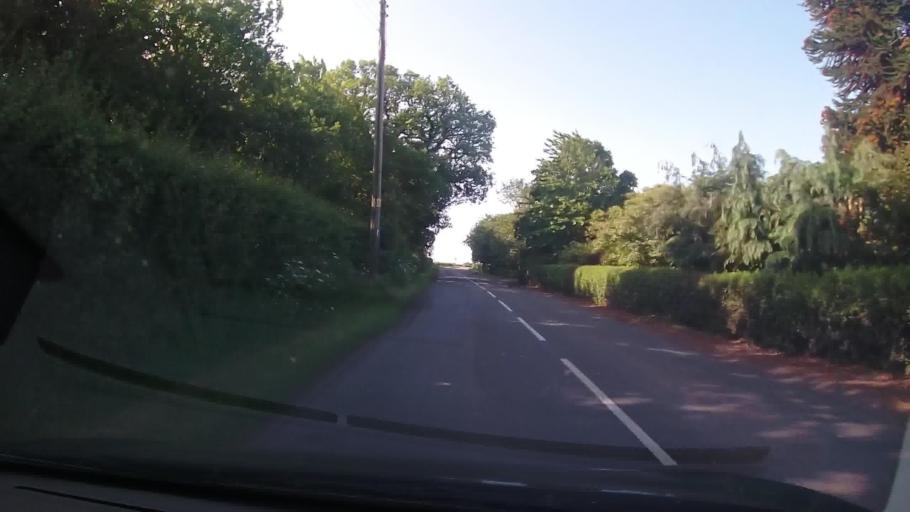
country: GB
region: England
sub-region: Shropshire
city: Withington
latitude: 52.7611
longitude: -2.6080
